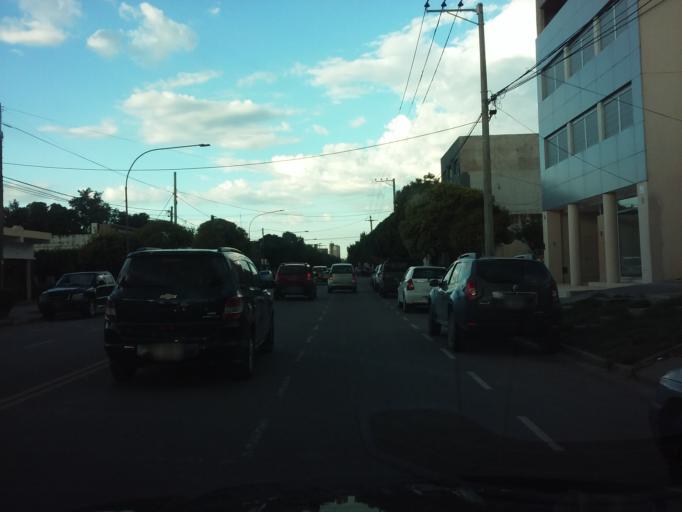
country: AR
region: La Pampa
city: Santa Rosa
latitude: -36.6291
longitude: -64.2922
